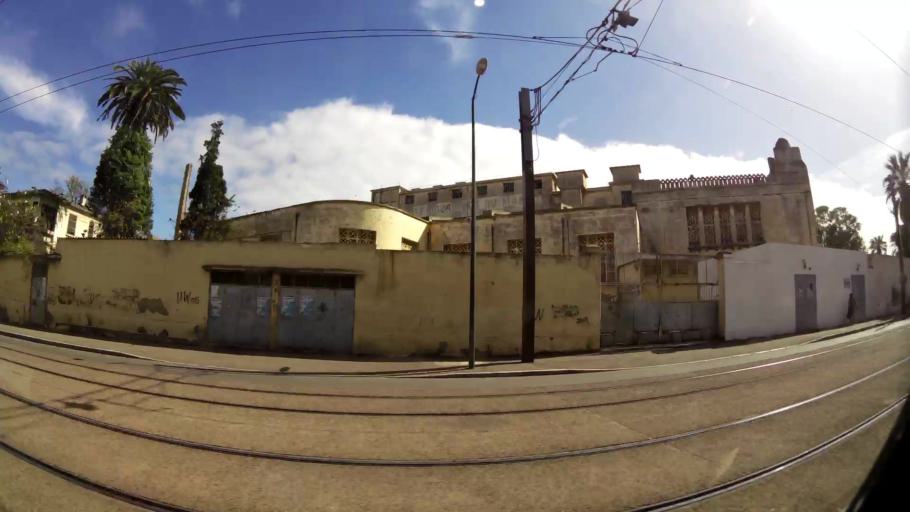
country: MA
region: Grand Casablanca
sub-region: Casablanca
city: Casablanca
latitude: 33.5939
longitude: -7.5832
